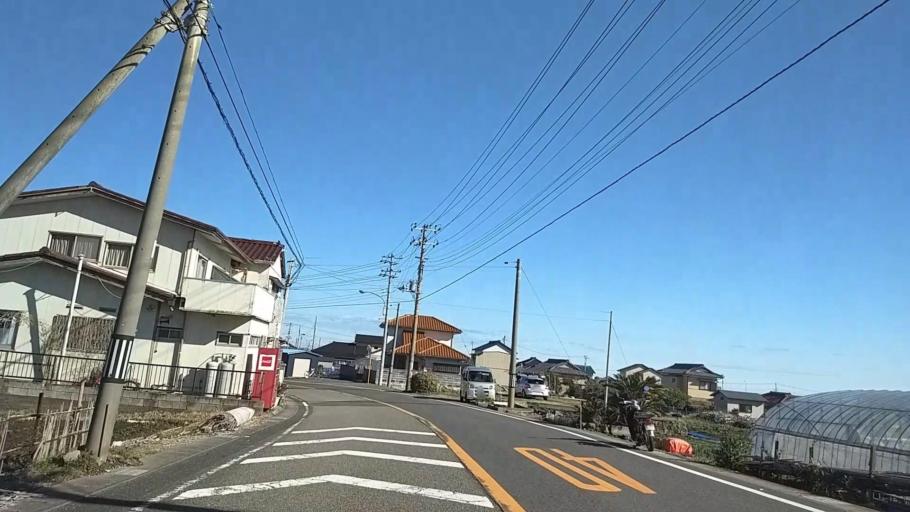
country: JP
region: Chiba
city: Tateyama
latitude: 34.9208
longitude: 139.9383
